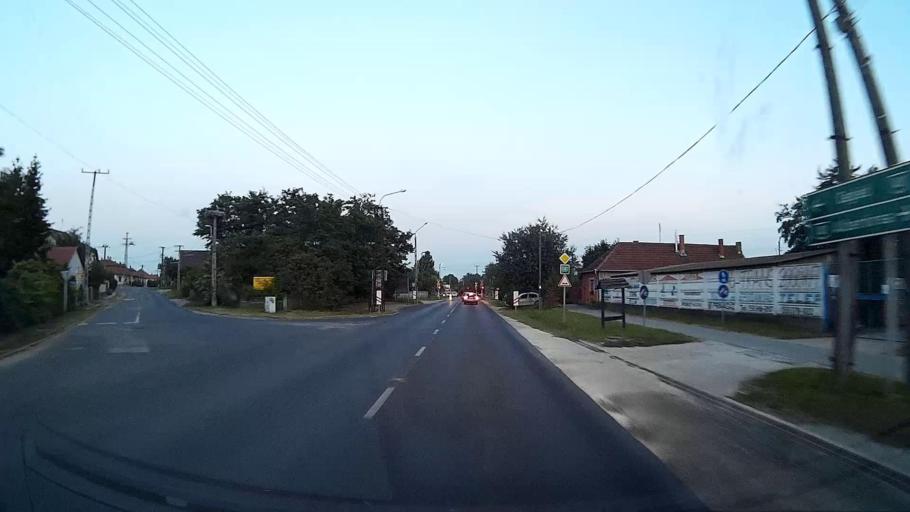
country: HU
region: Pest
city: Cegledbercel
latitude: 47.2122
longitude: 19.6799
